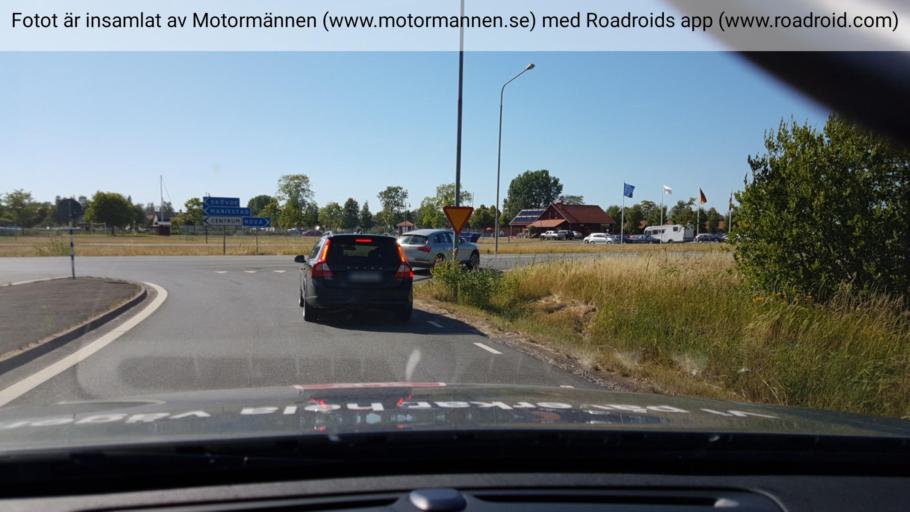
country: SE
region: Vaestra Goetaland
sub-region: Toreboda Kommun
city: Toereboda
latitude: 58.7127
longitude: 14.1318
